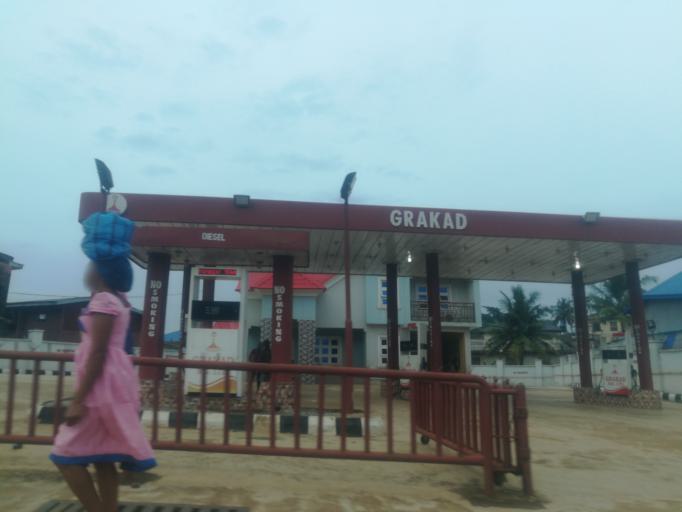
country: NG
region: Oyo
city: Egbeda
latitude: 7.3845
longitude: 3.9894
